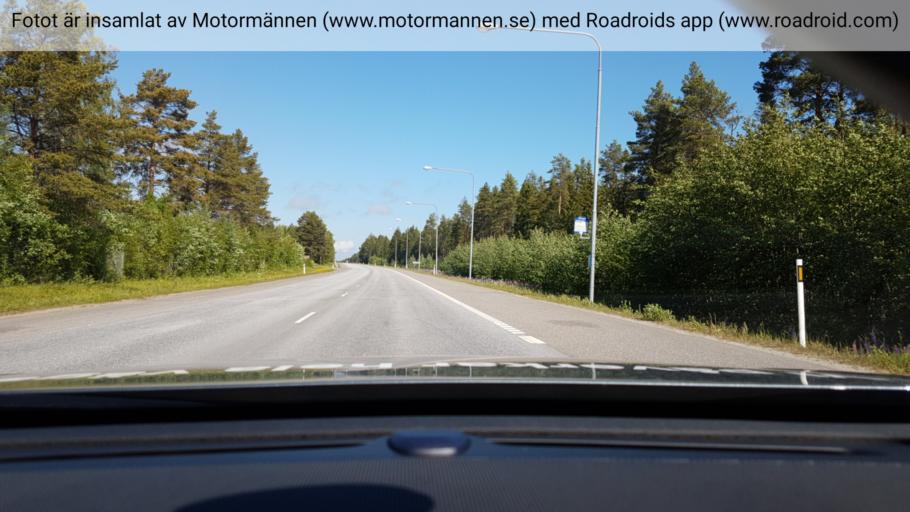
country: SE
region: Vaesterbotten
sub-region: Umea Kommun
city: Holmsund
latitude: 63.7281
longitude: 20.3901
